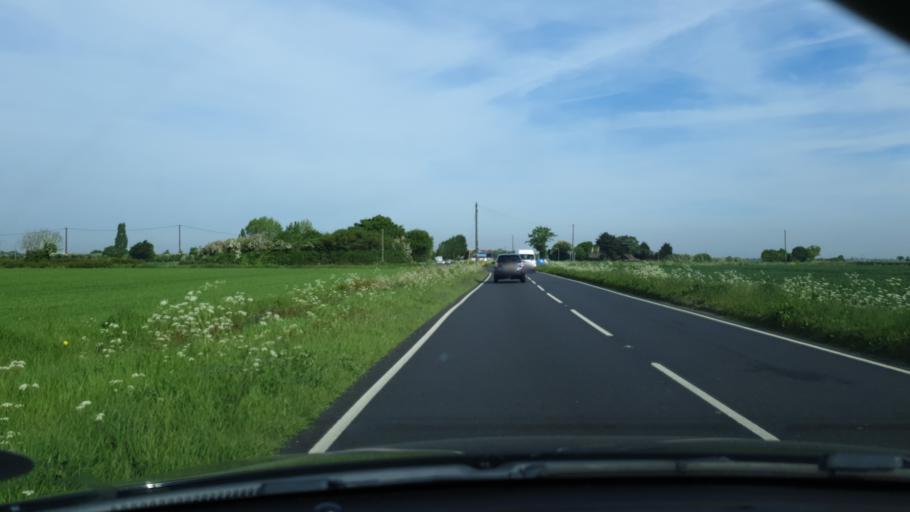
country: GB
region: England
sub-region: Essex
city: Little Clacton
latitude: 51.8490
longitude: 1.1907
